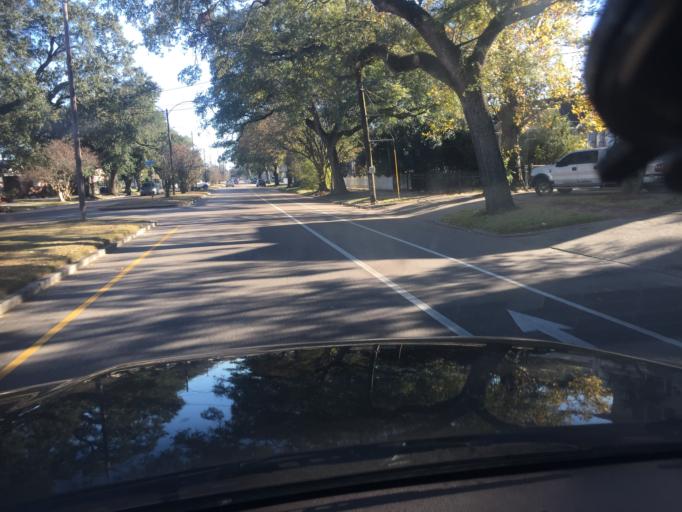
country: US
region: Louisiana
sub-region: Orleans Parish
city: New Orleans
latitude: 29.9871
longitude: -90.0740
